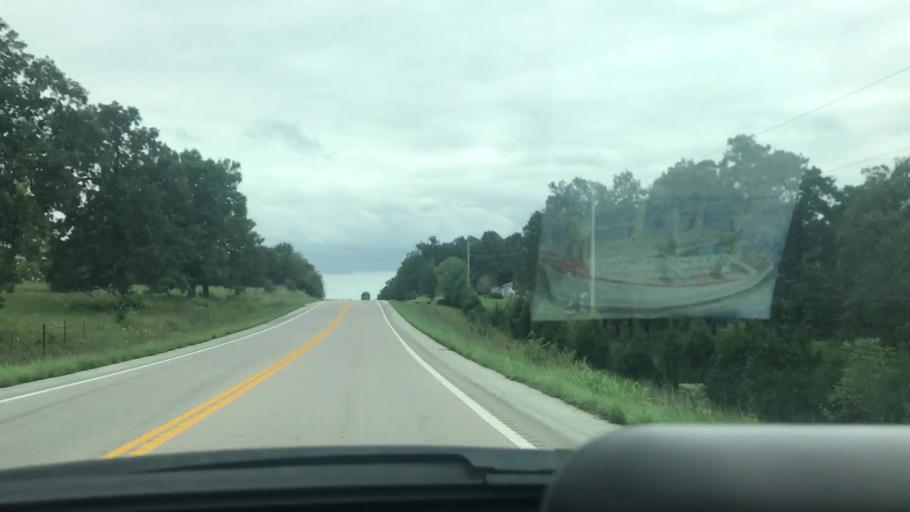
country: US
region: Missouri
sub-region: Dallas County
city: Buffalo
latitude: 37.7116
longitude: -93.1154
